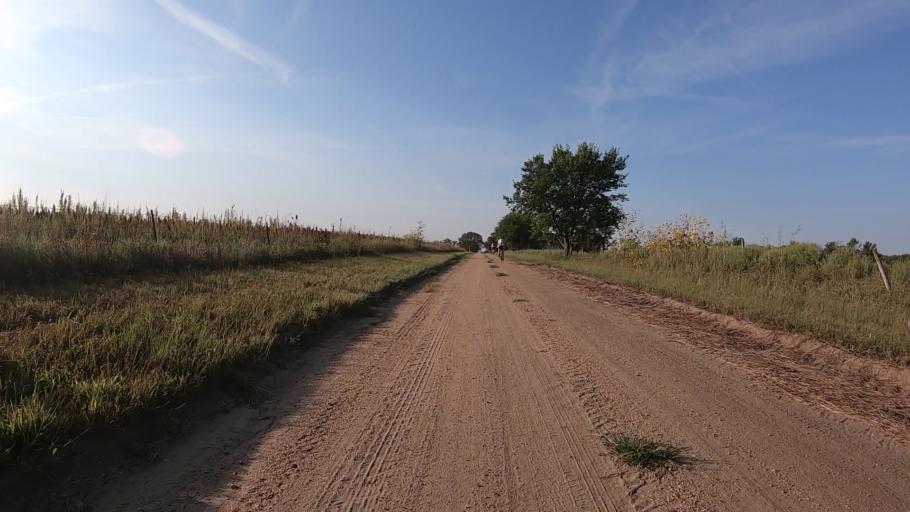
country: US
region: Kansas
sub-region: Marshall County
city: Blue Rapids
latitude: 39.7135
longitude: -96.8067
